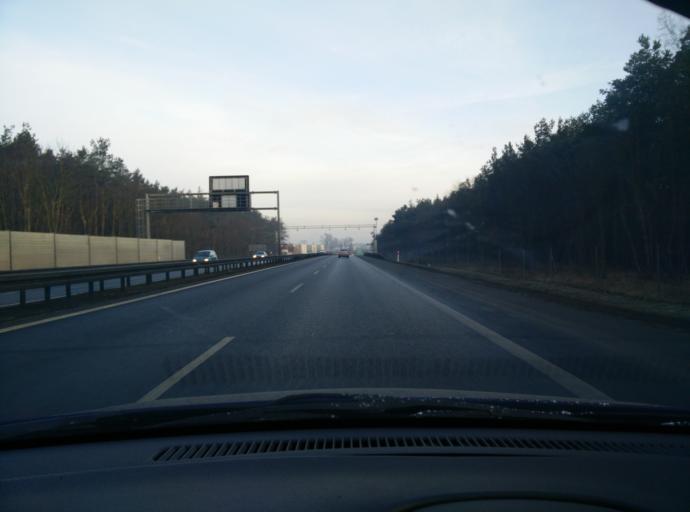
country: PL
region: Greater Poland Voivodeship
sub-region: Powiat poznanski
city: Kornik
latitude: 52.3039
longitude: 17.0481
